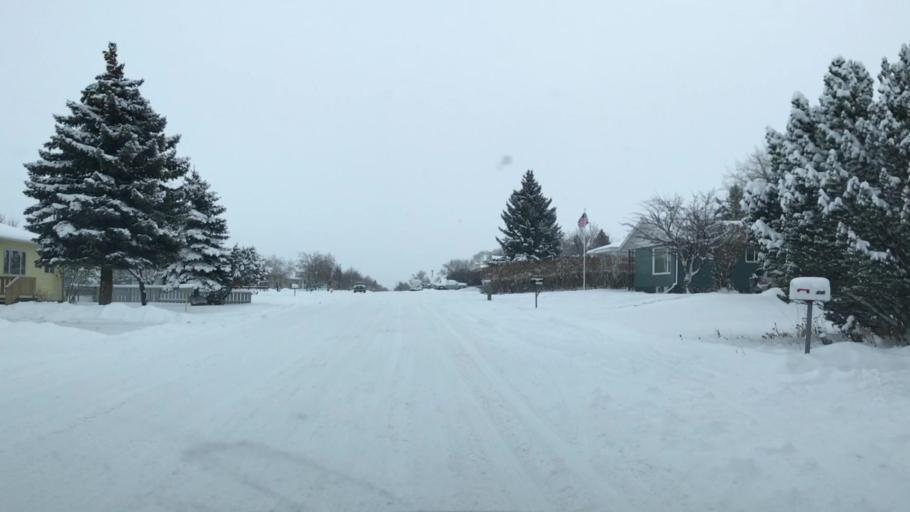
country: US
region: Montana
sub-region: Lewis and Clark County
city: Helena
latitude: 46.5932
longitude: -112.0142
